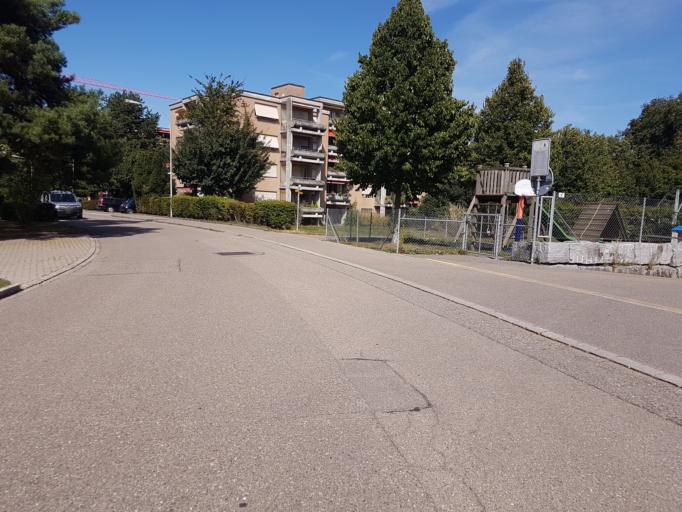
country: CH
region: Zurich
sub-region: Bezirk Pfaeffikon
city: Effretikon
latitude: 47.4246
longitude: 8.6883
